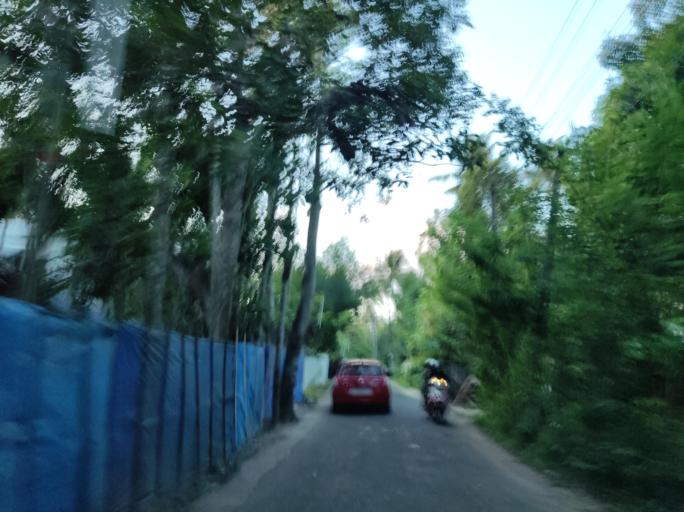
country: IN
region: Kerala
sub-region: Alappuzha
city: Vayalar
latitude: 9.7375
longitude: 76.2890
